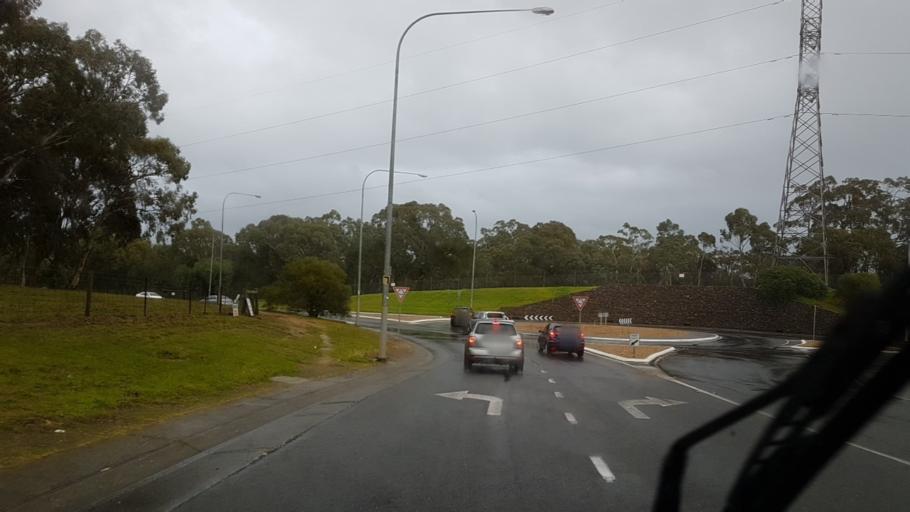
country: AU
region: South Australia
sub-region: Onkaparinga
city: Craigburn Farm
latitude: -35.0696
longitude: 138.5837
